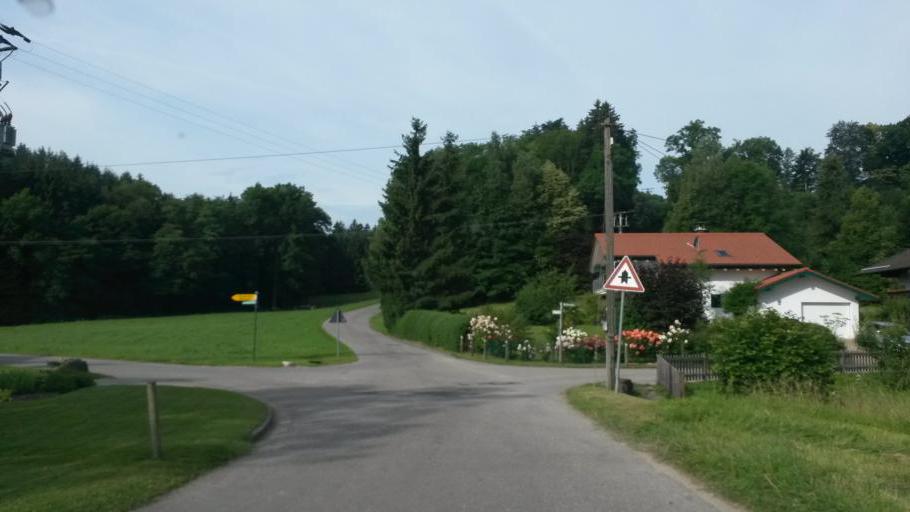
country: DE
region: Bavaria
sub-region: Upper Bavaria
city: Bernau am Chiemsee
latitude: 47.8264
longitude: 12.3532
